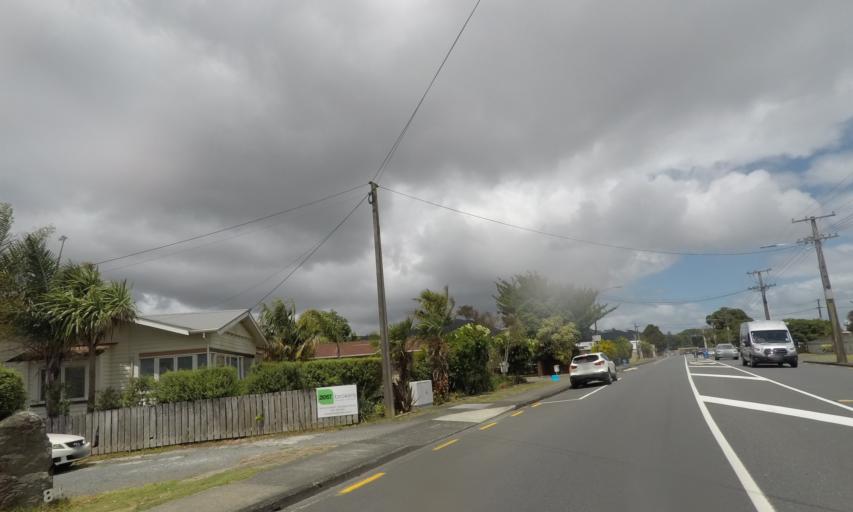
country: NZ
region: Northland
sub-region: Whangarei
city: Whangarei
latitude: -35.7056
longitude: 174.3194
